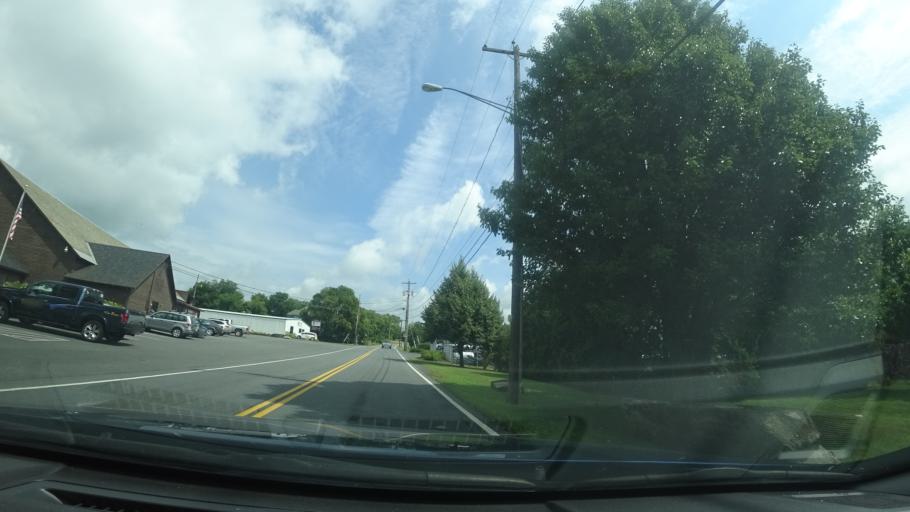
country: US
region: New York
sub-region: Saratoga County
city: South Glens Falls
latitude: 43.3110
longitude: -73.6116
